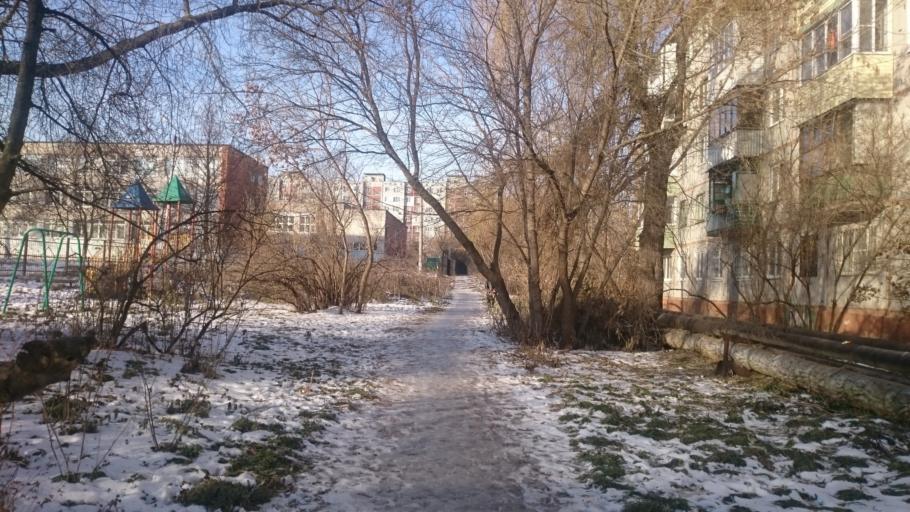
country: RU
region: Tula
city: Tula
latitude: 54.1770
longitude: 37.6380
